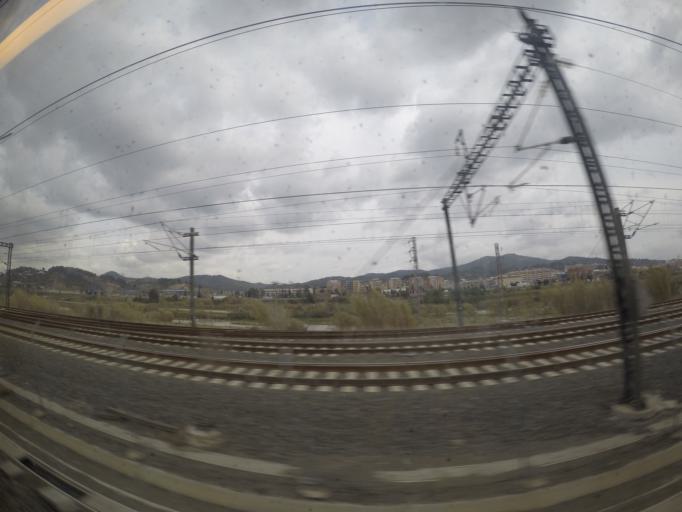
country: ES
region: Catalonia
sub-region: Provincia de Barcelona
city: Molins de Rei
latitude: 41.4149
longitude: 2.0069
